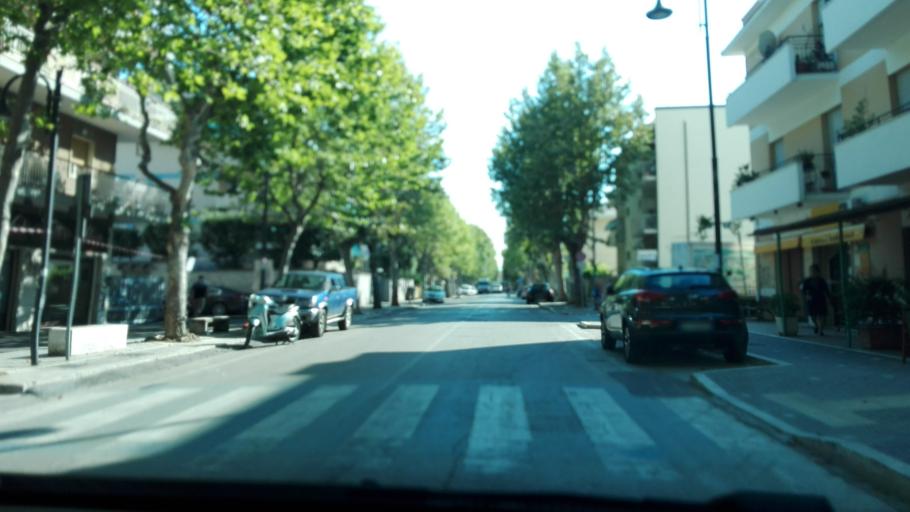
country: IT
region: Abruzzo
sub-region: Provincia di Pescara
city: Montesilvano Marina
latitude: 42.5162
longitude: 14.1600
